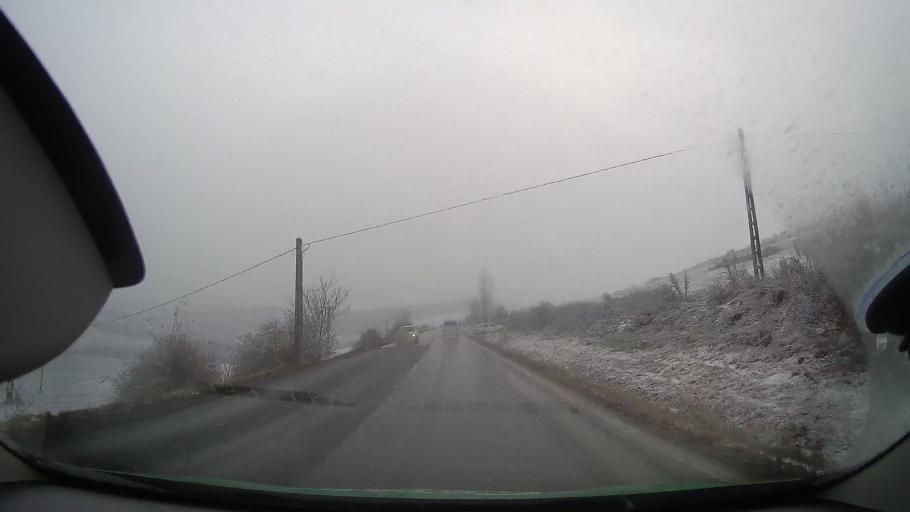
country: RO
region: Mures
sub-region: Comuna Bagaciu
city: Delenii
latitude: 46.2644
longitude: 24.3008
